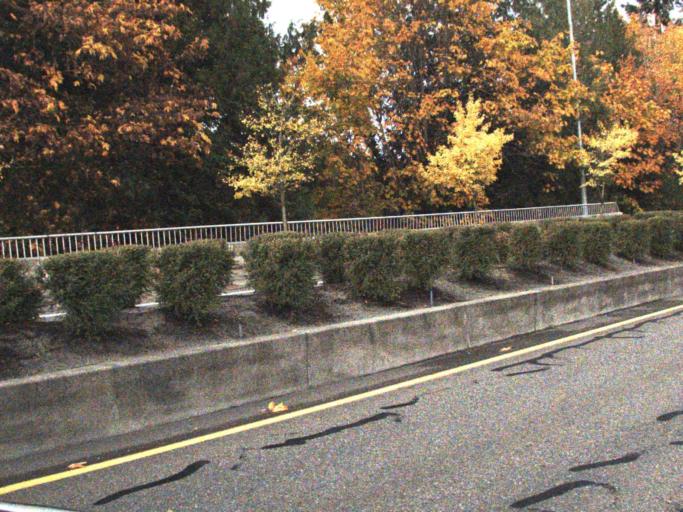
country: US
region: Washington
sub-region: Snohomish County
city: Mukilteo
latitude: 47.9025
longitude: -122.2929
